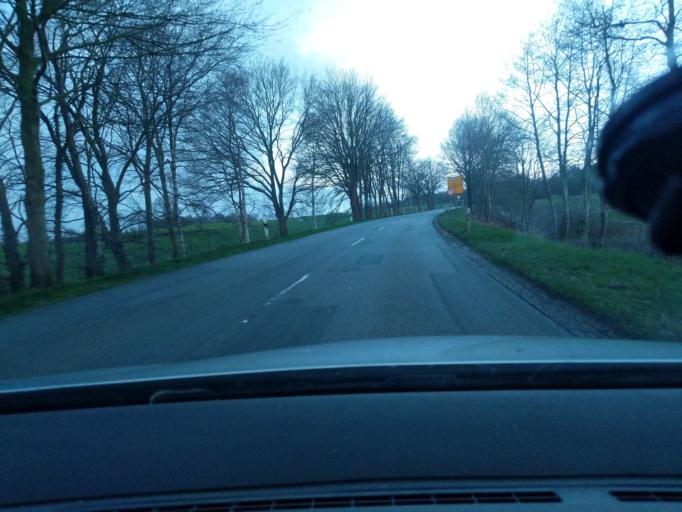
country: DE
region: Lower Saxony
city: Lintig
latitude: 53.6112
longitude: 8.8500
